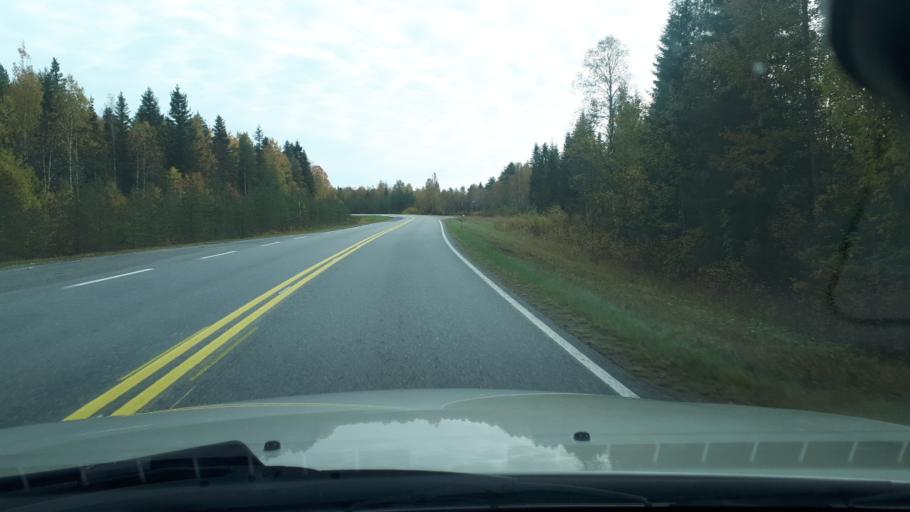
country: FI
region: Lapland
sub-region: Rovaniemi
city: Ranua
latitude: 66.0012
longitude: 26.2311
